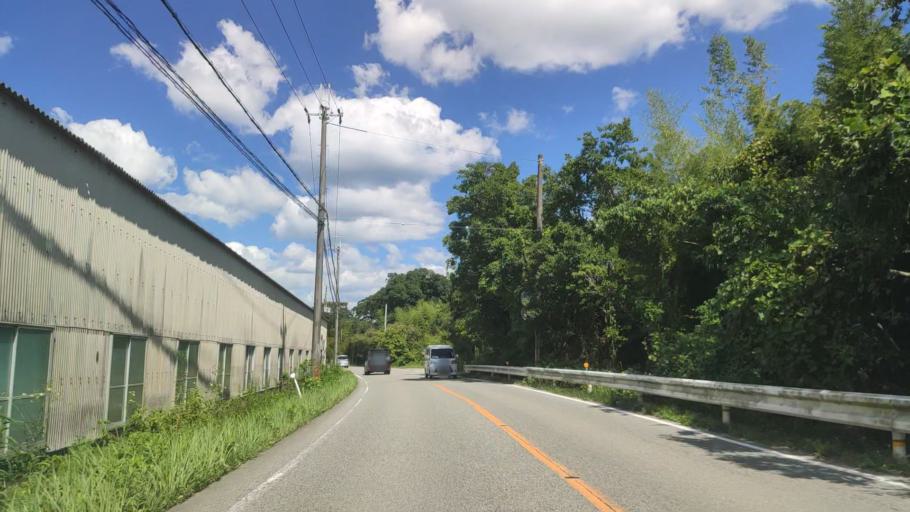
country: JP
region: Kyoto
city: Fukuchiyama
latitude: 35.1830
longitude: 135.1233
